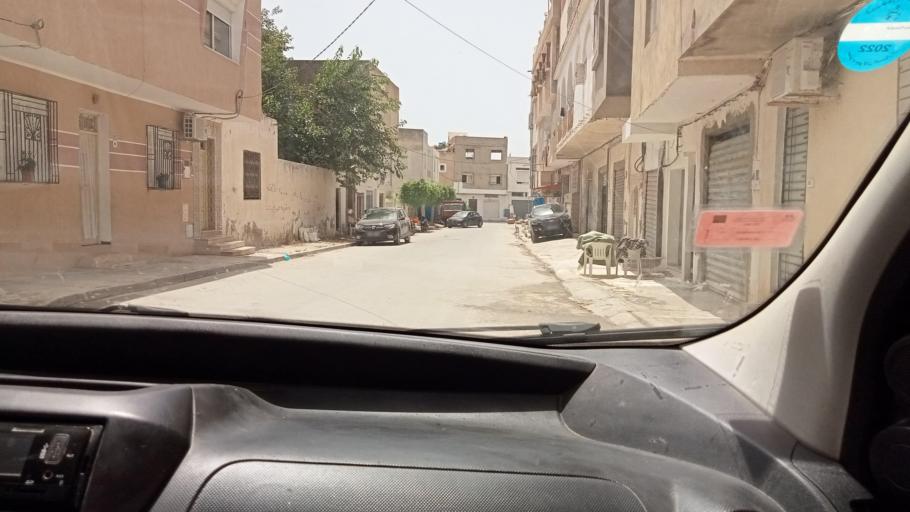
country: TN
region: Nabul
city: Qulaybiyah
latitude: 36.8526
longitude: 11.0892
